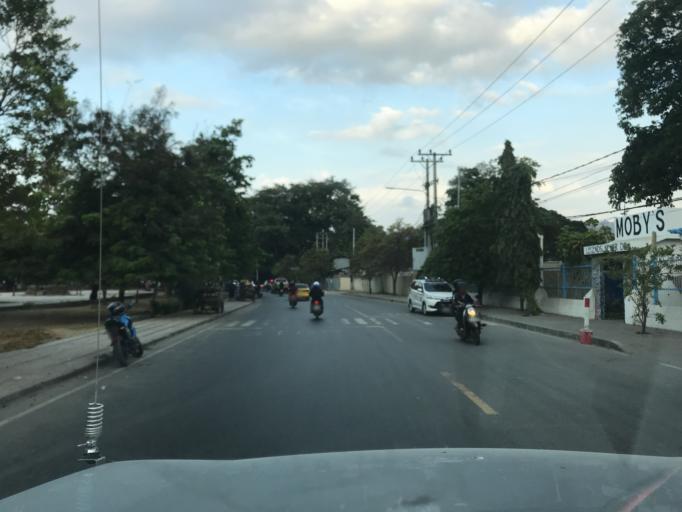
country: TL
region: Dili
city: Dili
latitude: -8.5518
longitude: 125.5824
